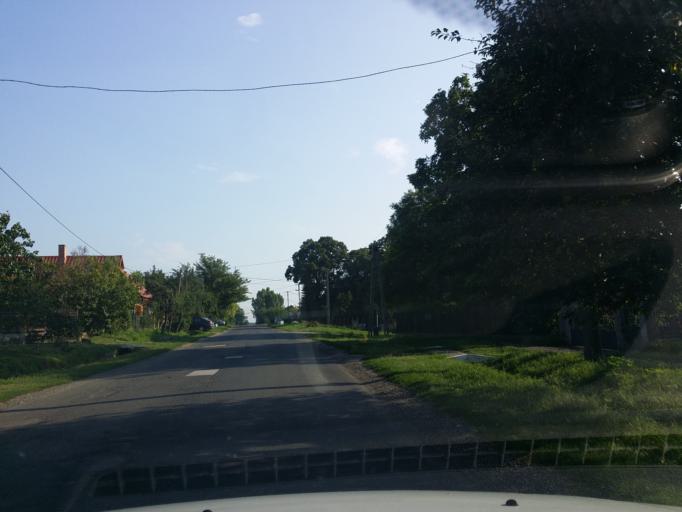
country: HU
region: Borsod-Abauj-Zemplen
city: Gonc
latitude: 48.4449
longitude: 21.2391
